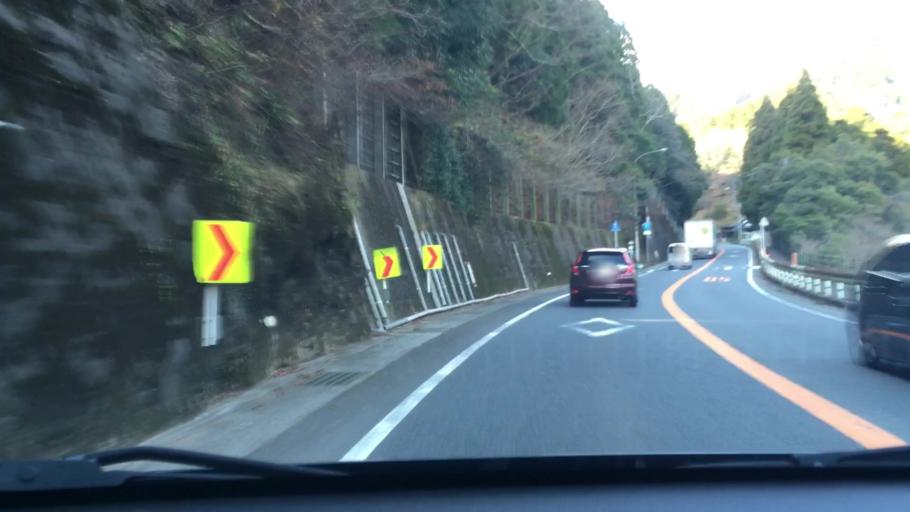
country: JP
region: Oita
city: Tsukumiura
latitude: 32.9992
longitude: 131.8143
